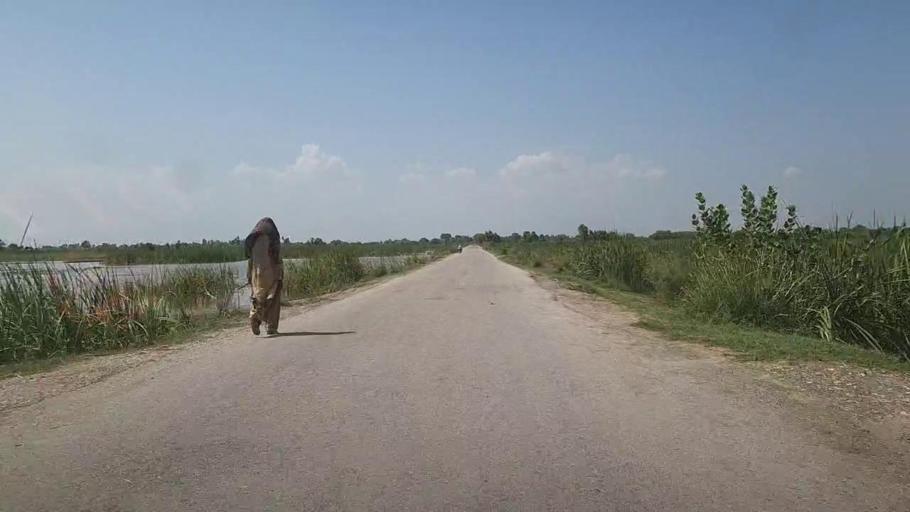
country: PK
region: Sindh
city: Khairpur
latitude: 28.0702
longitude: 69.6419
